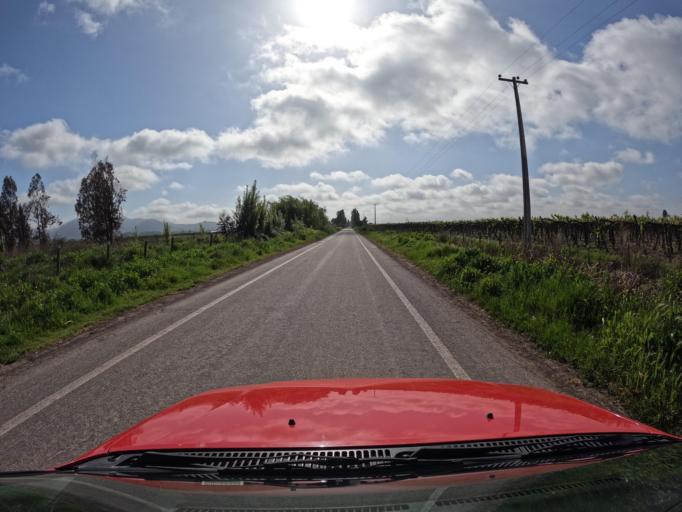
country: CL
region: Maule
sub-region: Provincia de Curico
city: Rauco
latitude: -34.8855
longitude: -71.2556
